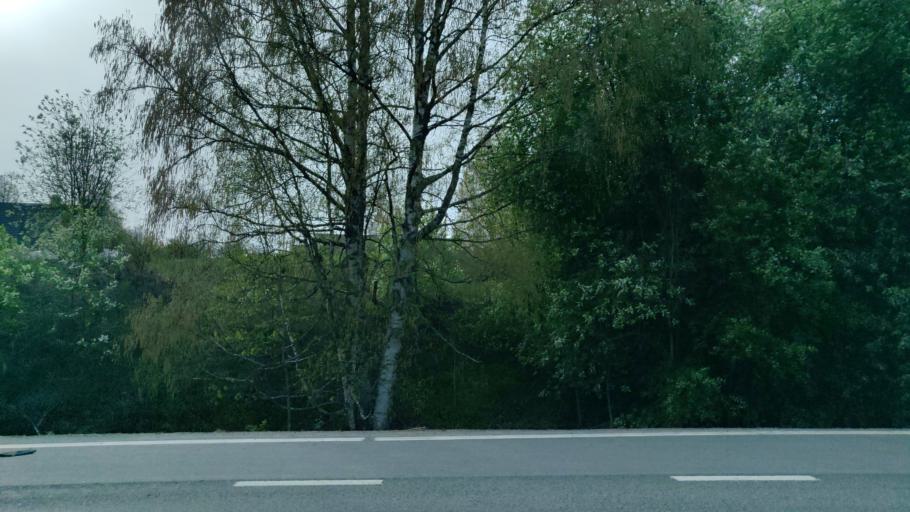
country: SE
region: Vaermland
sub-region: Munkfors Kommun
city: Munkfors
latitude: 59.8229
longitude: 13.5208
